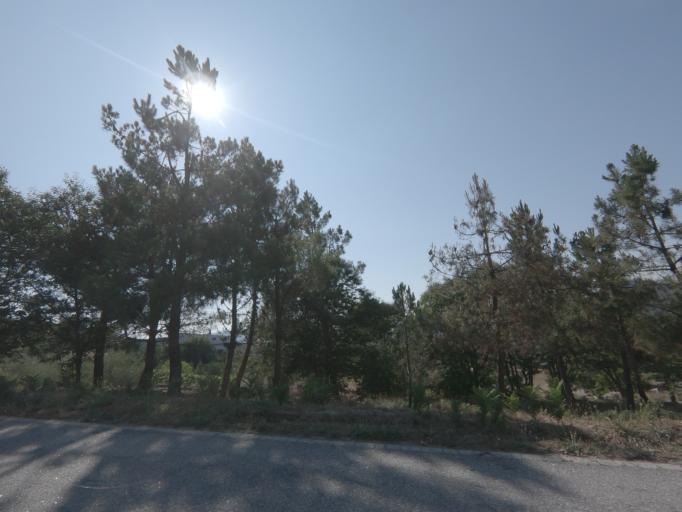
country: PT
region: Viseu
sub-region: Tabuaco
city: Tabuaco
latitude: 41.0456
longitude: -7.5705
